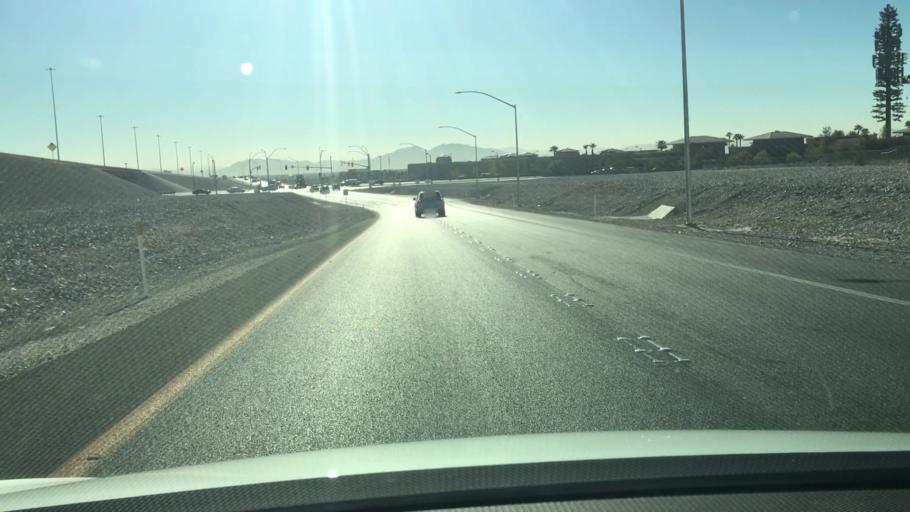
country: US
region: Nevada
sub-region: Clark County
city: Summerlin South
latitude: 36.2796
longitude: -115.2907
